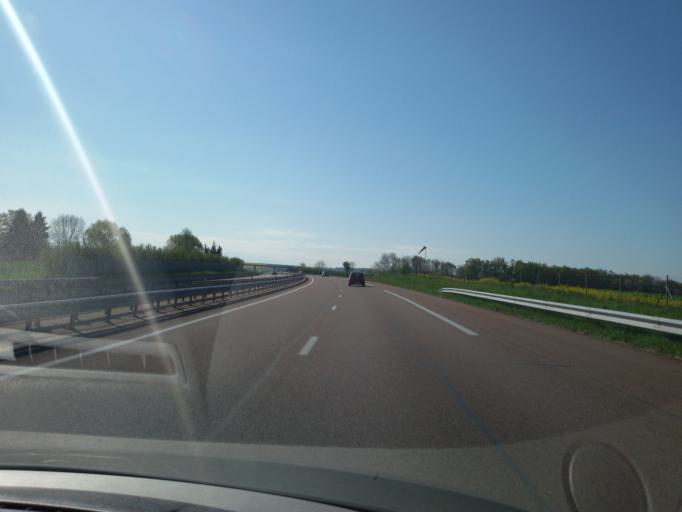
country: FR
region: Bourgogne
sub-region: Departement de l'Yonne
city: Venoy
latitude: 47.8068
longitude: 3.6309
